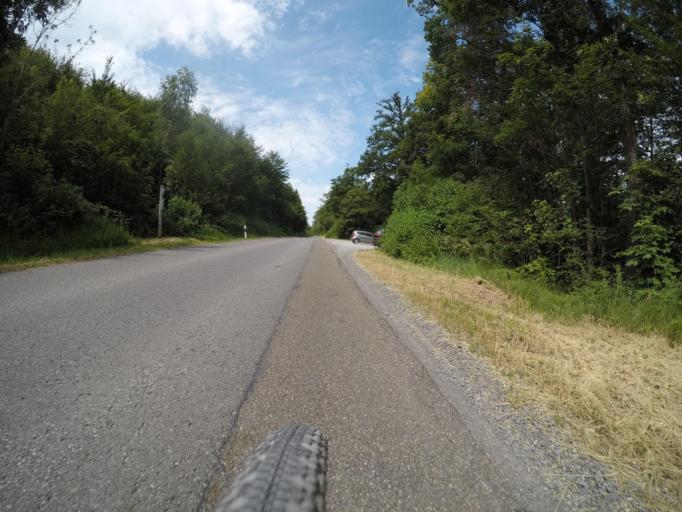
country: DE
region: Baden-Wuerttemberg
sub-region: Regierungsbezirk Stuttgart
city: Gerlingen
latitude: 48.7815
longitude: 9.1024
